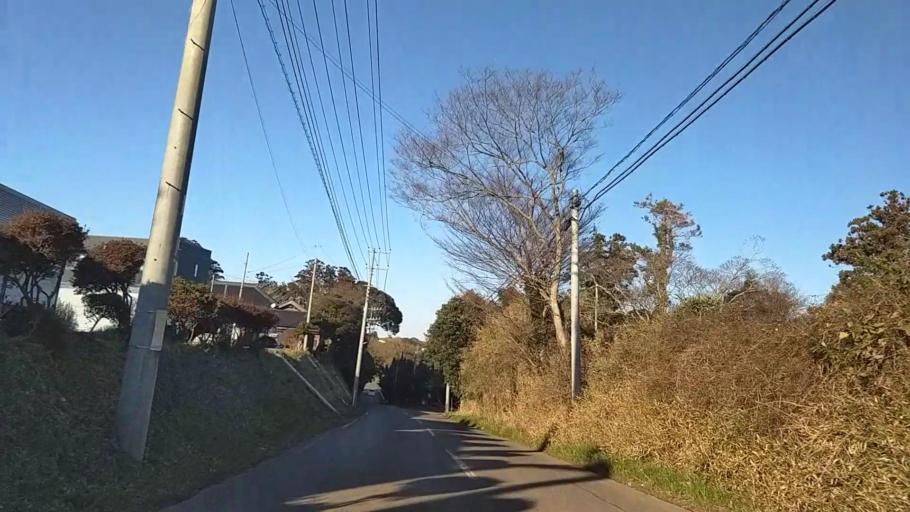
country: JP
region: Chiba
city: Asahi
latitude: 35.7233
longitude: 140.7356
